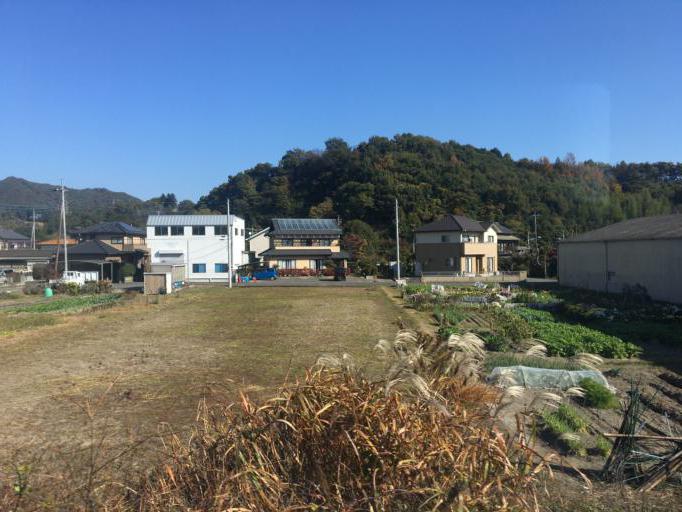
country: JP
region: Gunma
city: Kiryu
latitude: 36.3791
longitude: 139.3696
